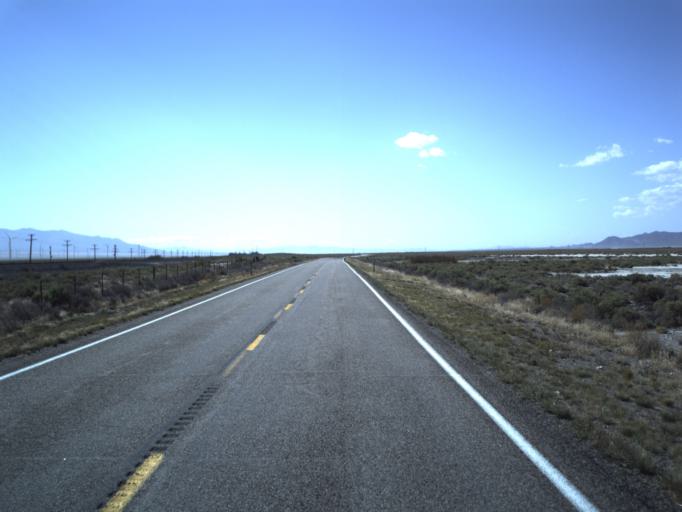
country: US
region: Utah
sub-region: Beaver County
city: Milford
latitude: 38.6112
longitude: -112.9860
